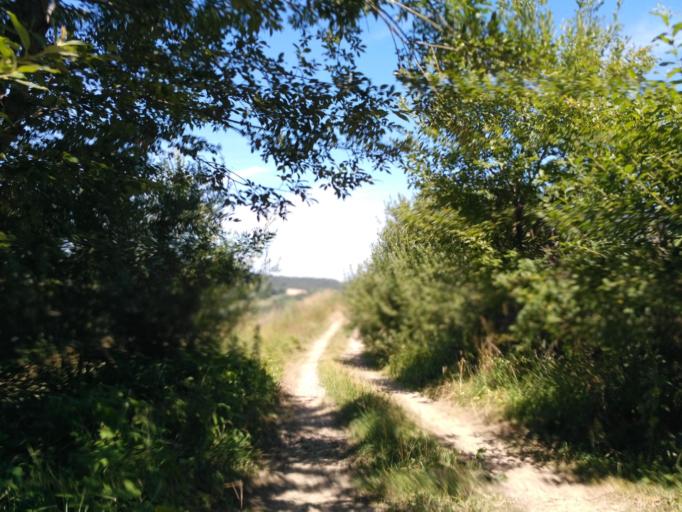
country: PL
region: Subcarpathian Voivodeship
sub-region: Powiat sanocki
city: Bukowsko
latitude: 49.4890
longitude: 22.0713
